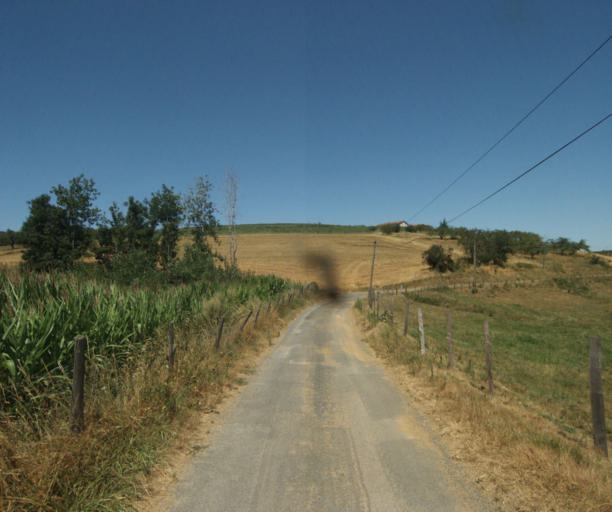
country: FR
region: Rhone-Alpes
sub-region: Departement du Rhone
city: Bessenay
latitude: 45.7659
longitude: 4.5290
